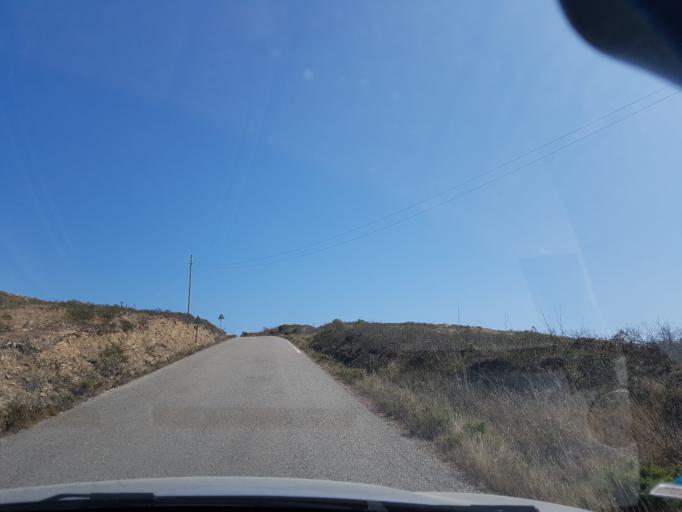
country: PT
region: Faro
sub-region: Vila do Bispo
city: Vila do Bispo
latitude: 37.0954
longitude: -8.9338
